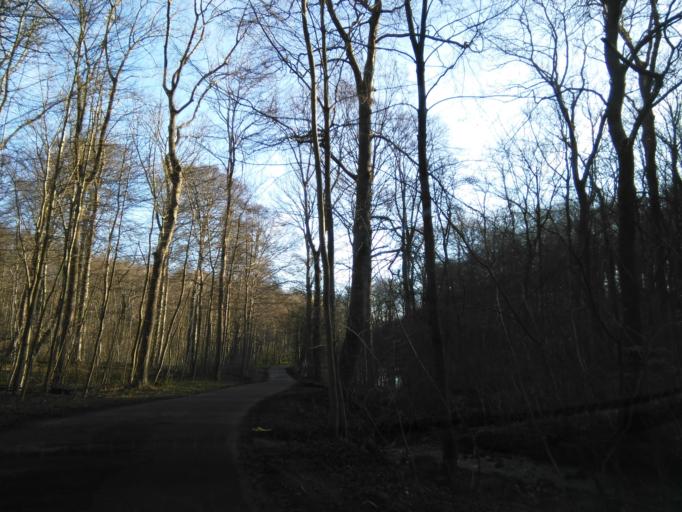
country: DK
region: Central Jutland
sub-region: Arhus Kommune
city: Arhus
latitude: 56.1196
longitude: 10.2100
